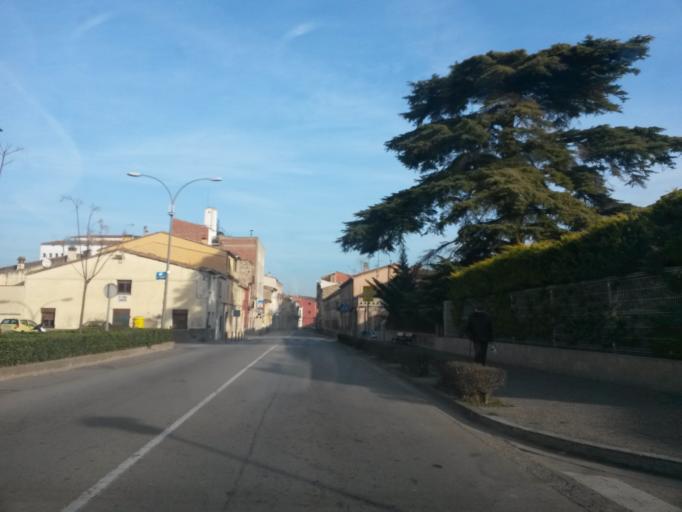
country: ES
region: Catalonia
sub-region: Provincia de Girona
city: Sarria de Ter
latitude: 42.0103
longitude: 2.8252
